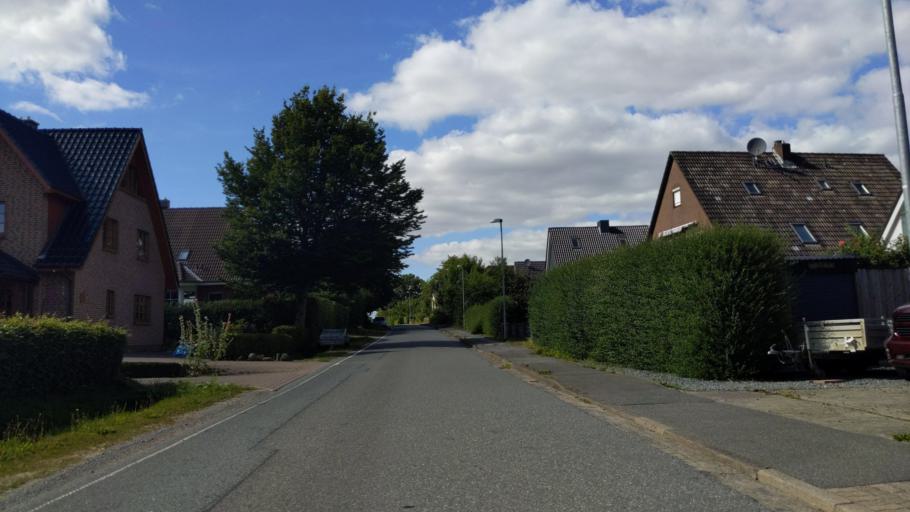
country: DE
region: Schleswig-Holstein
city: Stockelsdorf
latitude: 53.9316
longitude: 10.6035
